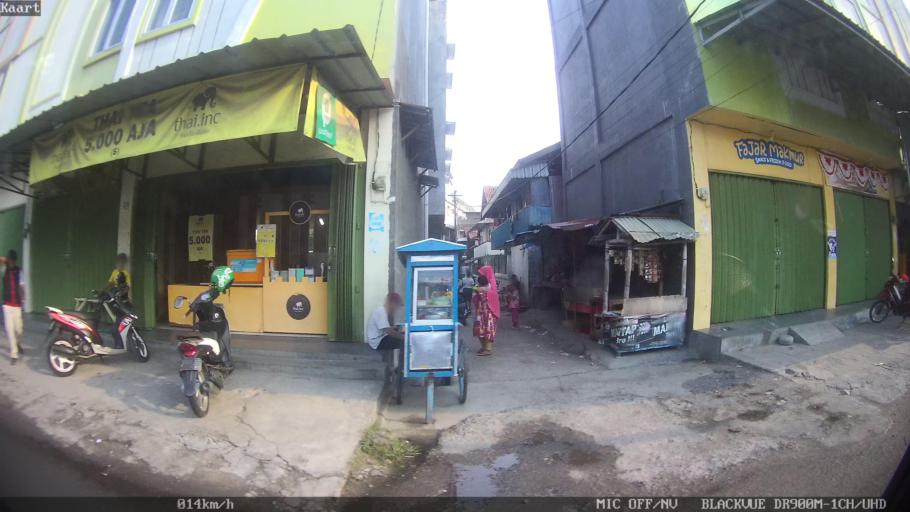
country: ID
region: Lampung
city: Bandarlampung
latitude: -5.4468
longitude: 105.2649
